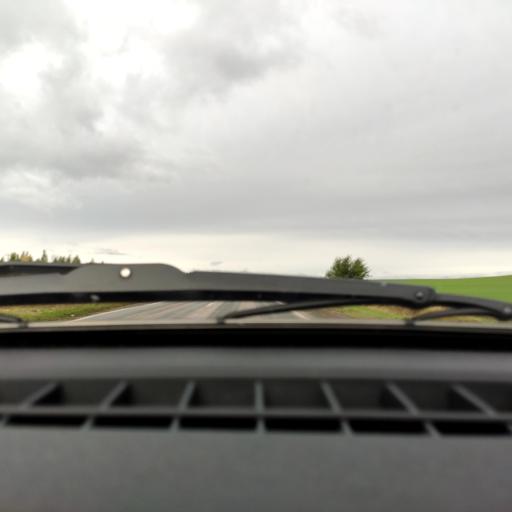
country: RU
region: Bashkortostan
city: Rayevskiy
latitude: 54.1490
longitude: 54.9486
